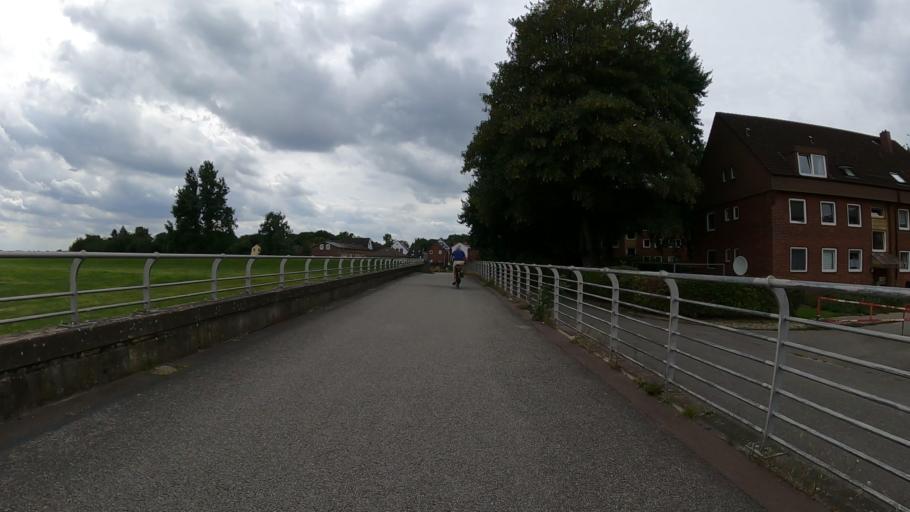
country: DE
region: Hamburg
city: Altona
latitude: 53.5288
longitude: 9.8884
